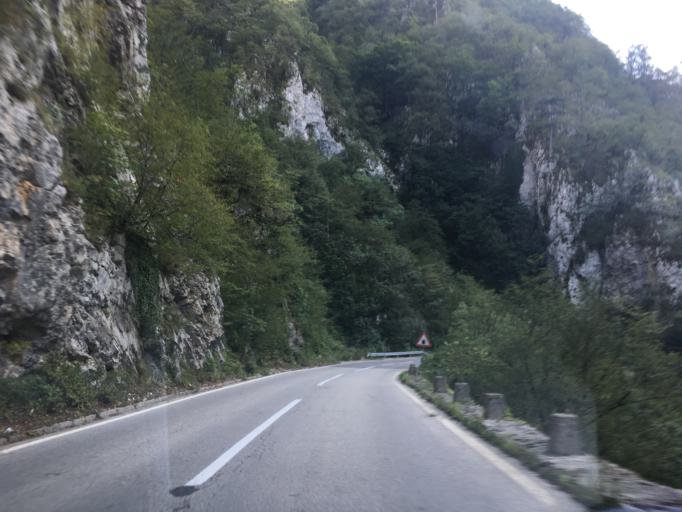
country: ME
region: Opstina Pluzine
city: Pluzine
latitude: 43.2959
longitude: 18.8541
